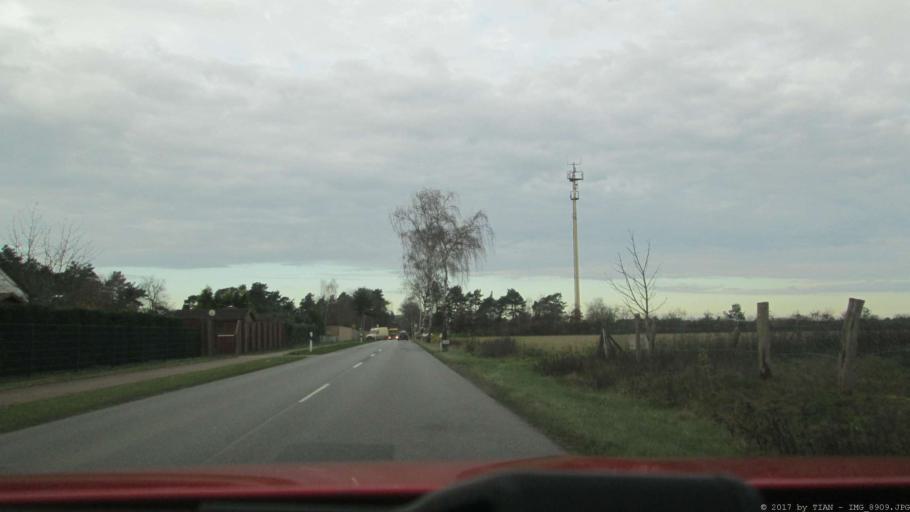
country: DE
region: Lower Saxony
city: Bokensdorf
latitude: 52.5509
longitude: 10.6911
